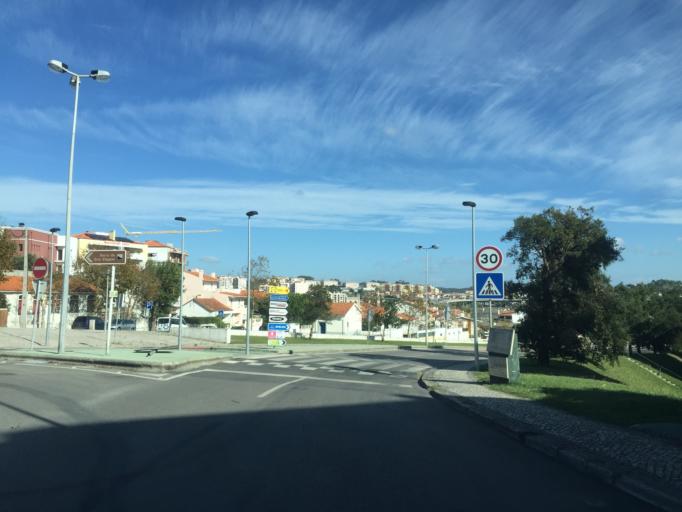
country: PT
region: Coimbra
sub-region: Figueira da Foz
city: Tavarede
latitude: 40.1643
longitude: -8.8514
